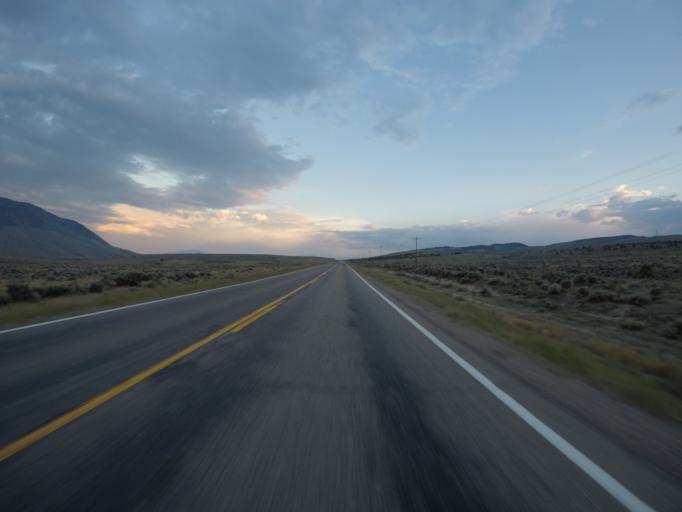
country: US
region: Colorado
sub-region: Grand County
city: Kremmling
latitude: 40.1256
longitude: -106.4300
